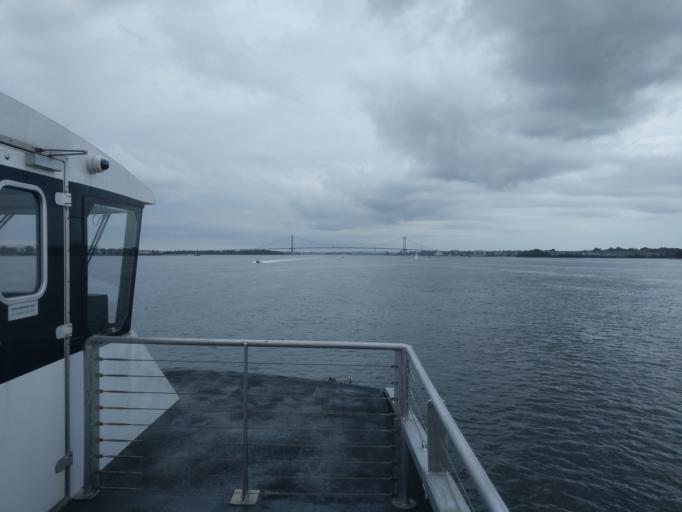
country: US
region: New York
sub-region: Bronx
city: The Bronx
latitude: 40.7991
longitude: -73.8663
